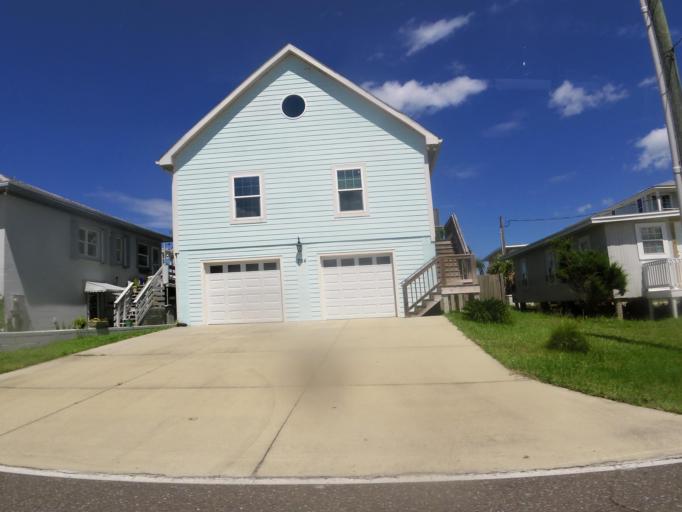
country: US
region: Florida
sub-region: Nassau County
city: Fernandina Beach
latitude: 30.6766
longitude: -81.4303
